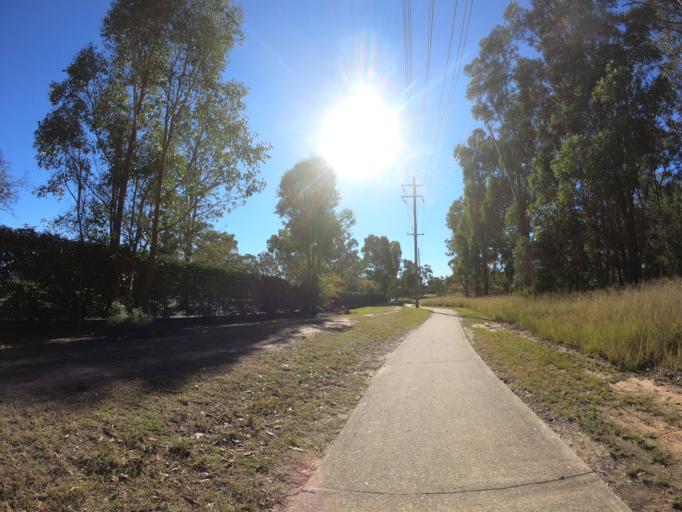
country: AU
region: New South Wales
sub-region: Hawkesbury
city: South Windsor
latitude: -33.6324
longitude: 150.7948
